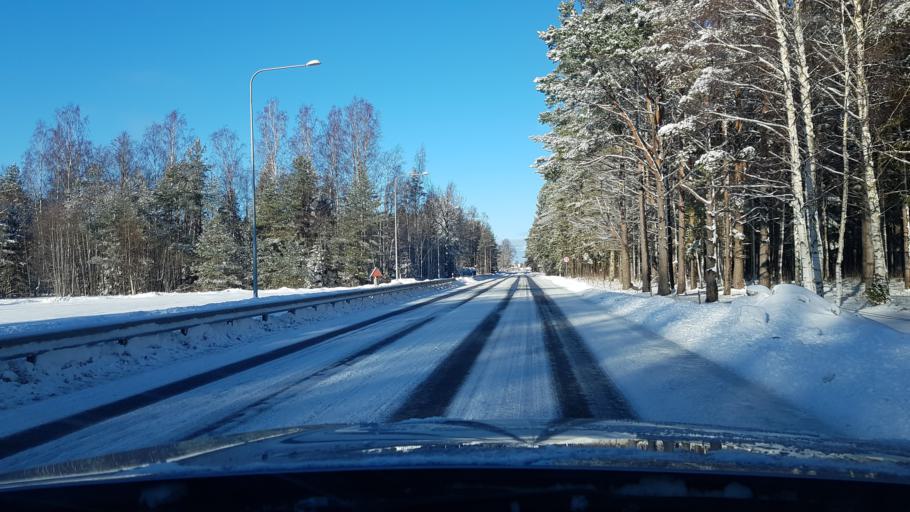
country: EE
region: Hiiumaa
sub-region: Kaerdla linn
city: Kardla
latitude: 58.9798
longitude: 22.7595
